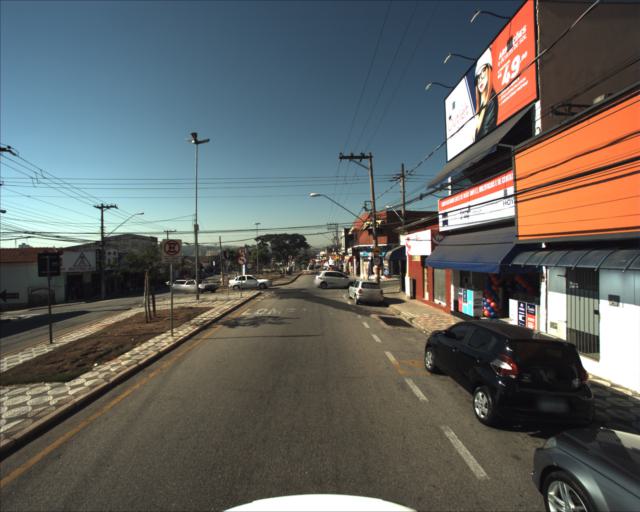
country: BR
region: Sao Paulo
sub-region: Sorocaba
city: Sorocaba
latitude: -23.5076
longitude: -47.4412
